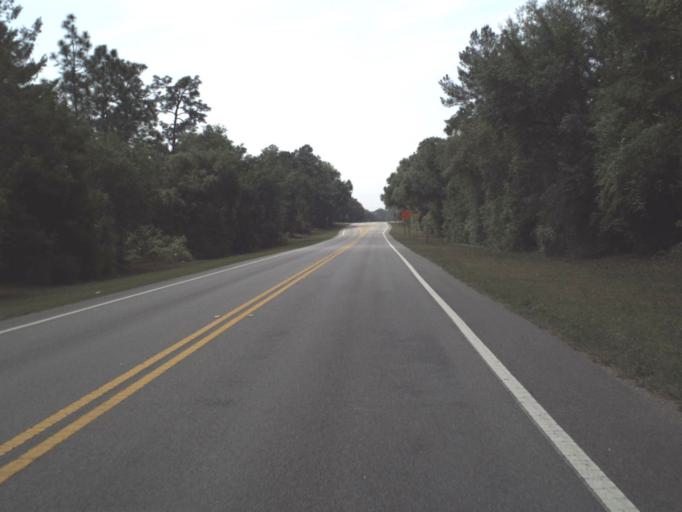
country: US
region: Florida
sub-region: Putnam County
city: Crescent City
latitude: 29.3632
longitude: -81.7355
